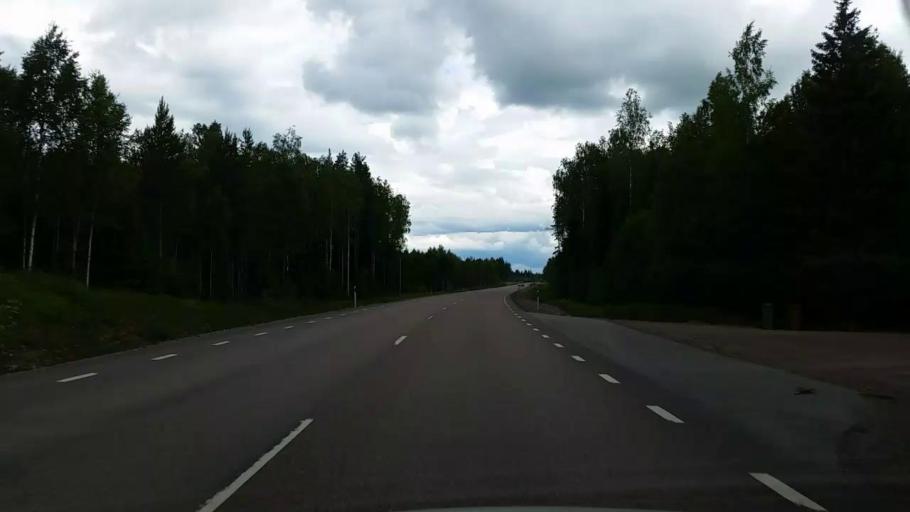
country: SE
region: Gaevleborg
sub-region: Hofors Kommun
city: Hofors
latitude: 60.4808
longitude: 16.4442
